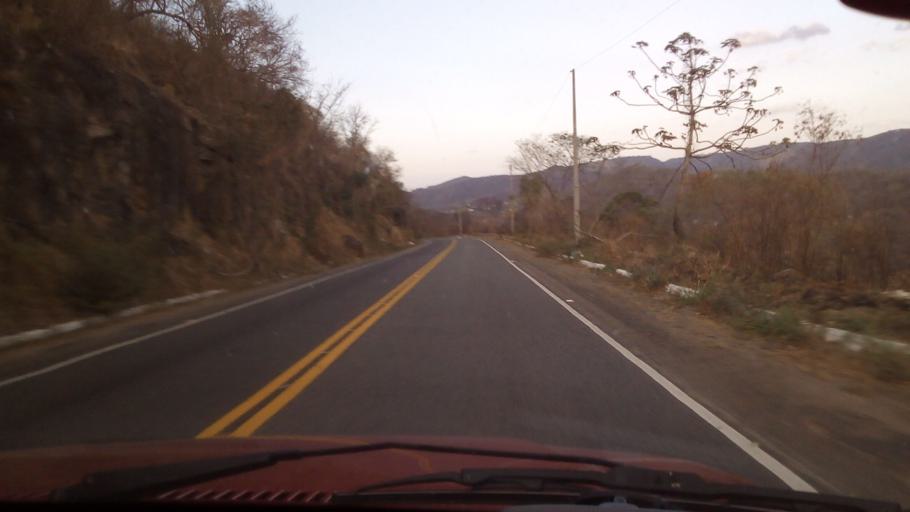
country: BR
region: Paraiba
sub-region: Bananeiras
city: Solanea
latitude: -6.7360
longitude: -35.5575
